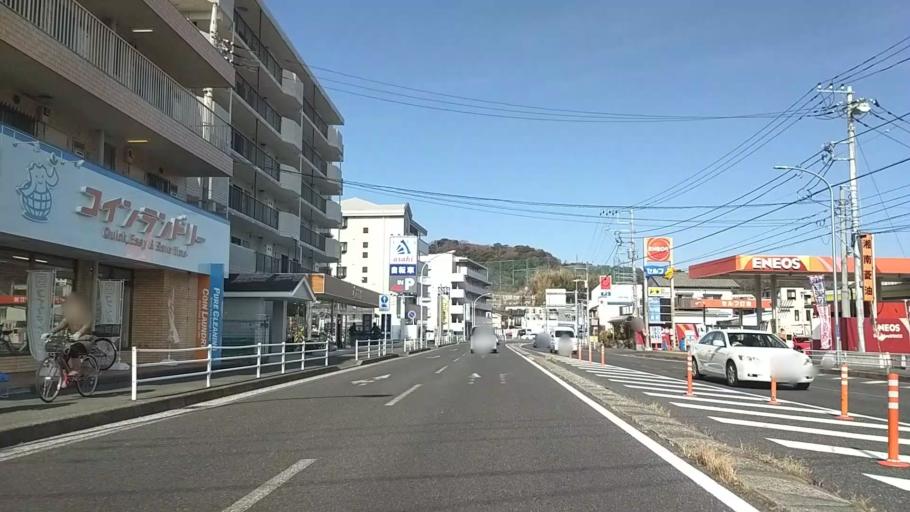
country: JP
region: Kanagawa
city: Zushi
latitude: 35.3456
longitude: 139.6098
